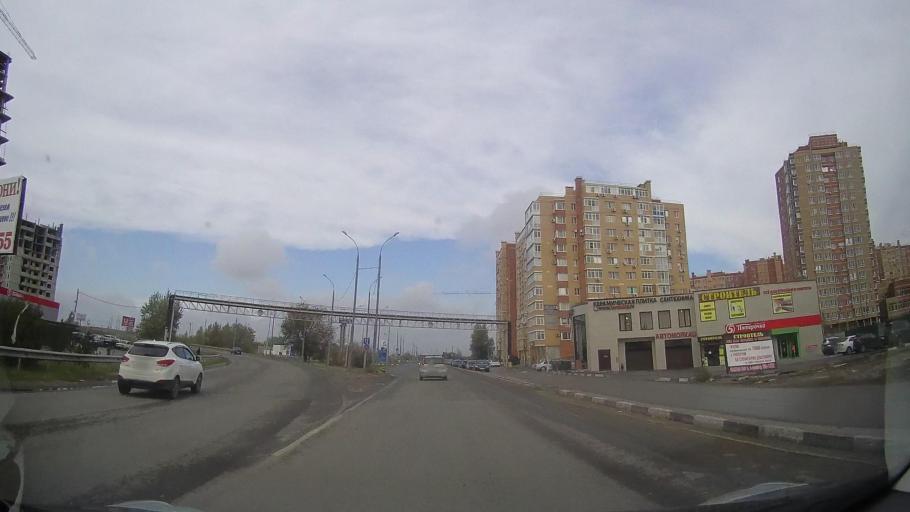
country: RU
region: Rostov
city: Bataysk
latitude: 47.1563
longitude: 39.7460
